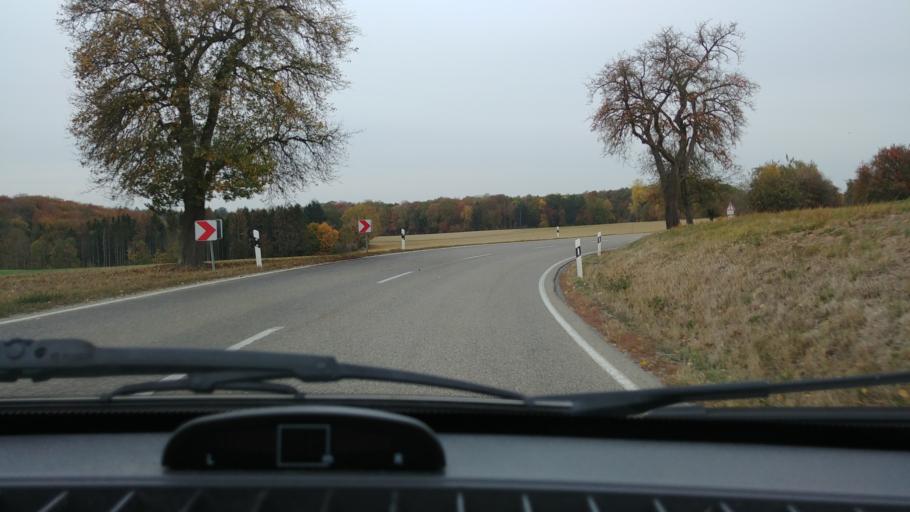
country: DE
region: Baden-Wuerttemberg
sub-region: Regierungsbezirk Stuttgart
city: Wallhausen
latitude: 49.2151
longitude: 10.0617
